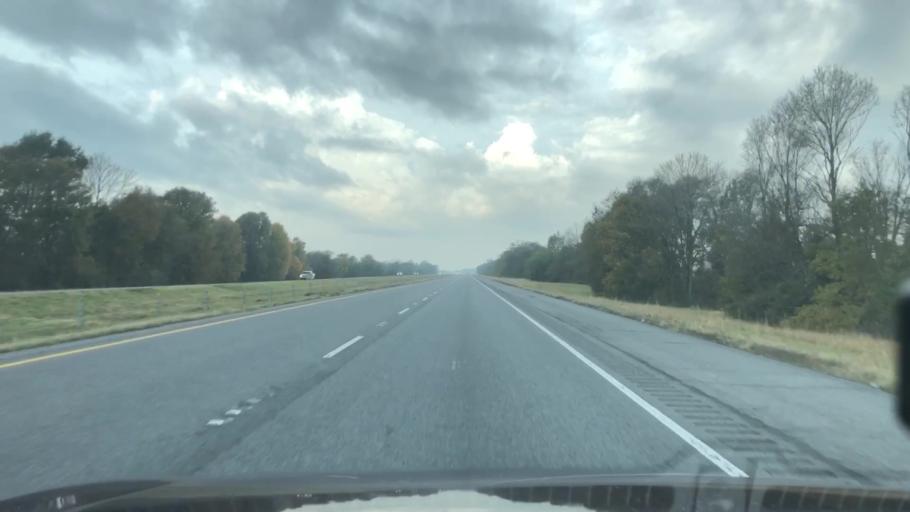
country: US
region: Louisiana
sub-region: Madison Parish
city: Tallulah
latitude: 32.4111
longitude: -91.2556
